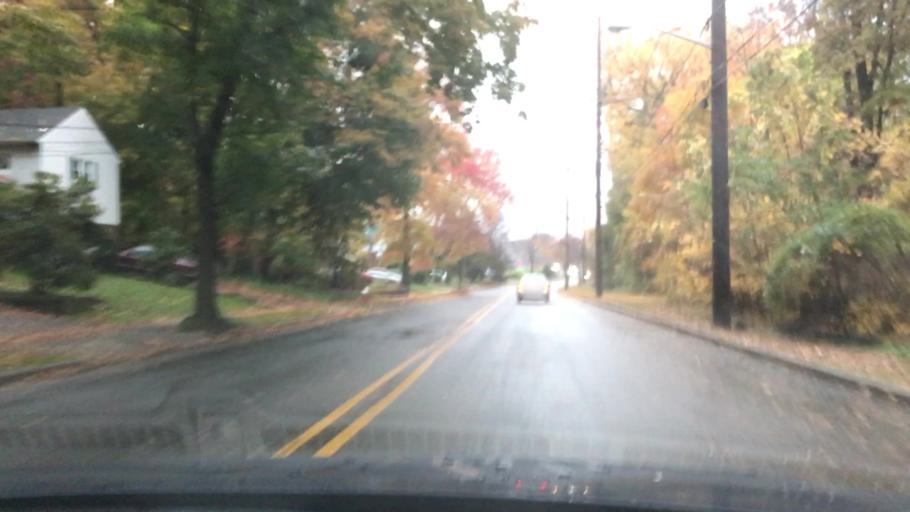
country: US
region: New Jersey
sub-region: Bergen County
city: Teaneck
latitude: 40.8960
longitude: -74.0134
